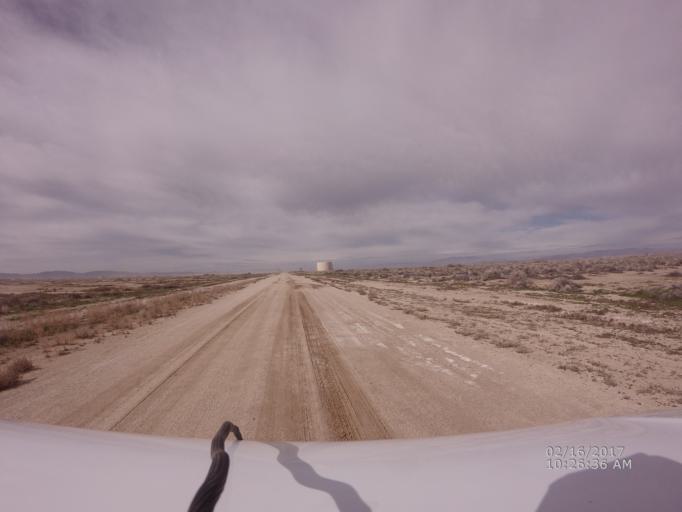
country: US
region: California
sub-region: Los Angeles County
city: Lake Los Angeles
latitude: 34.7342
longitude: -117.9544
